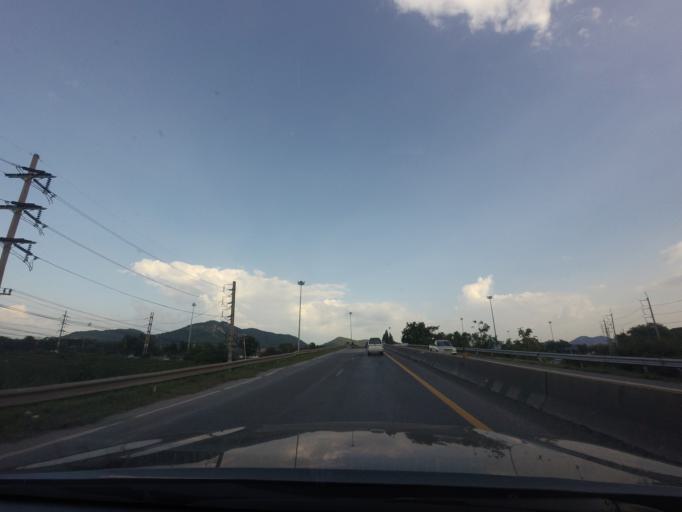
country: TH
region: Sara Buri
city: Saraburi
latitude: 14.5021
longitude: 100.9161
